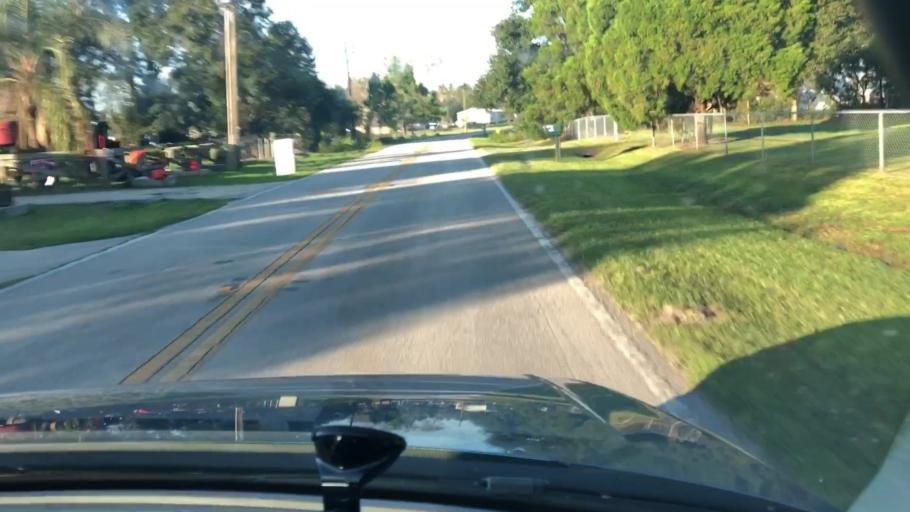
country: US
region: Florida
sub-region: Polk County
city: Kathleen
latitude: 28.1228
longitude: -82.0500
